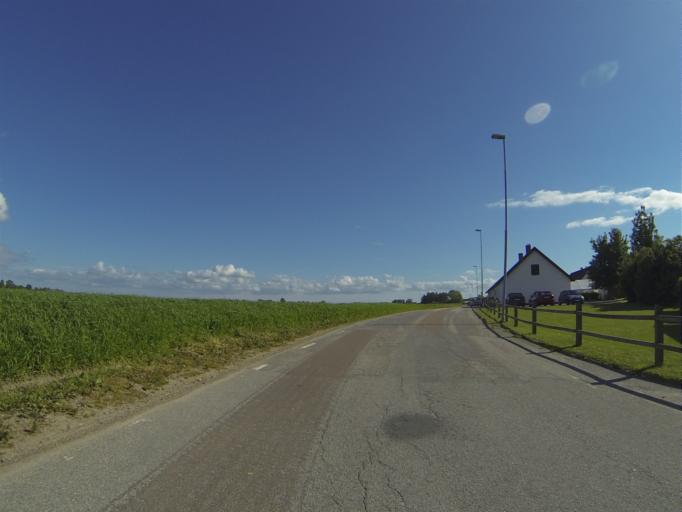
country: SE
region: Skane
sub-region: Staffanstorps Kommun
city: Staffanstorp
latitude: 55.6747
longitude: 13.2024
